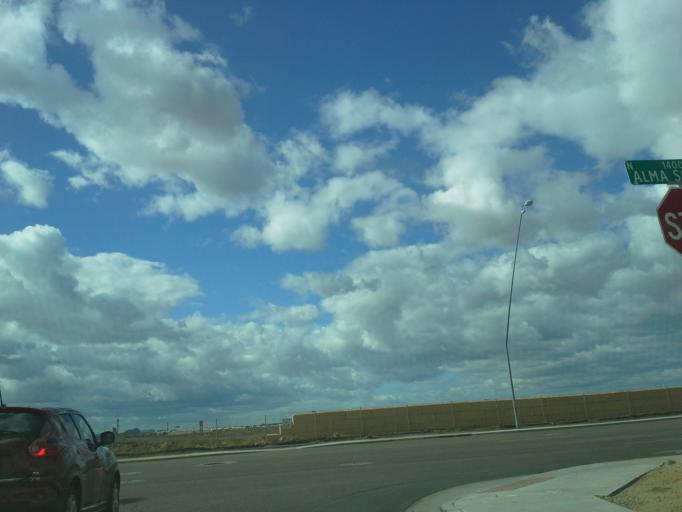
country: US
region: Arizona
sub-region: Maricopa County
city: Mesa
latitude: 33.4396
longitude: -111.8560
